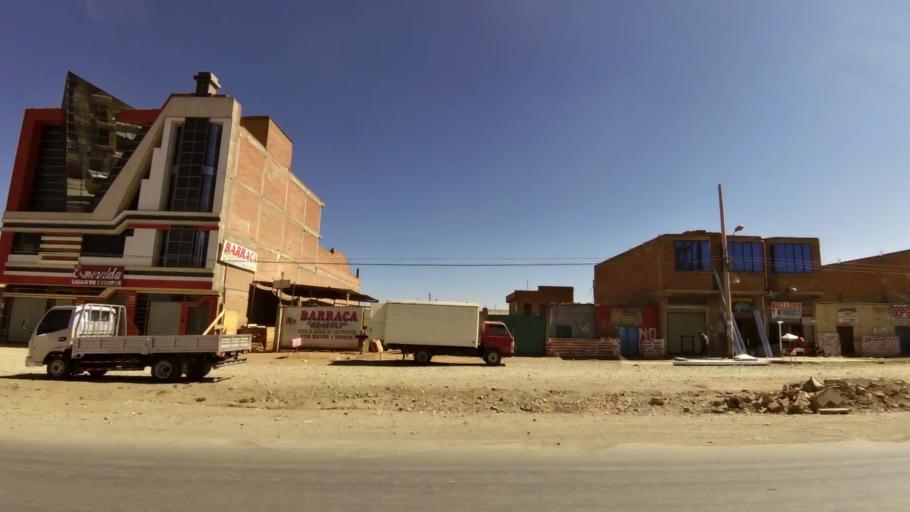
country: BO
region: La Paz
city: La Paz
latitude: -16.5443
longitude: -68.1998
